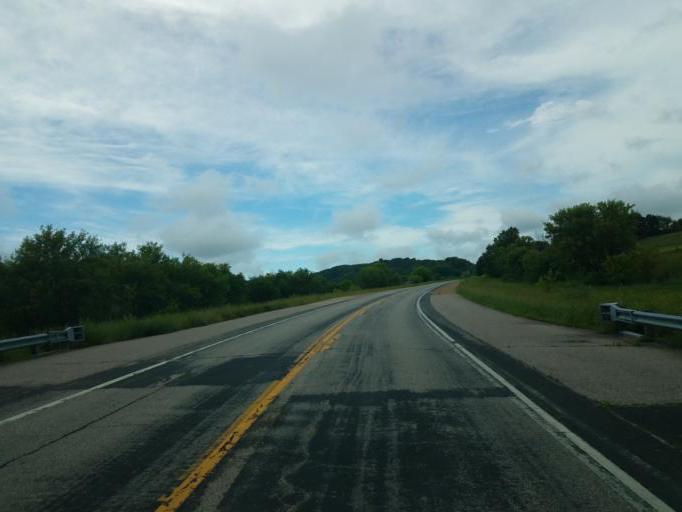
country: US
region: Wisconsin
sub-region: Vernon County
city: Hillsboro
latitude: 43.6567
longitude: -90.3942
